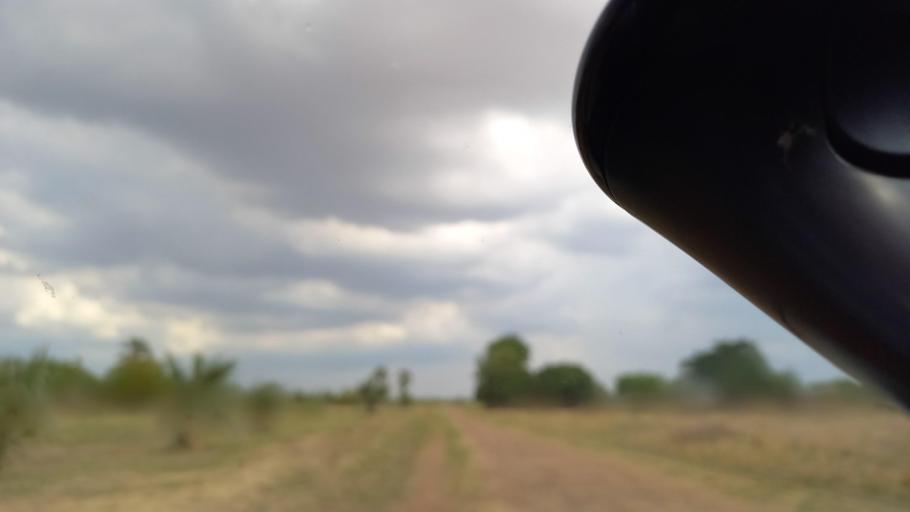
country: ZM
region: Lusaka
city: Kafue
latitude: -15.8374
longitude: 28.0840
